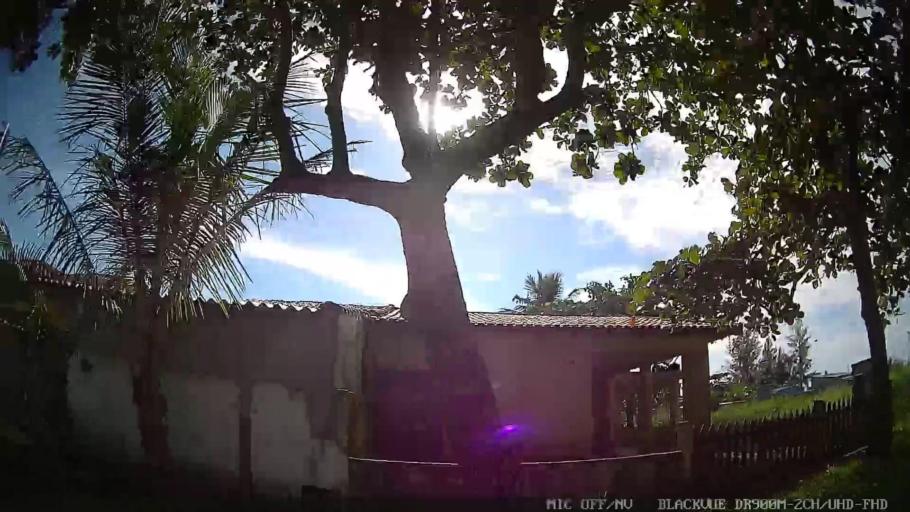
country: BR
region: Sao Paulo
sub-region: Iguape
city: Iguape
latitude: -24.7680
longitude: -47.5849
